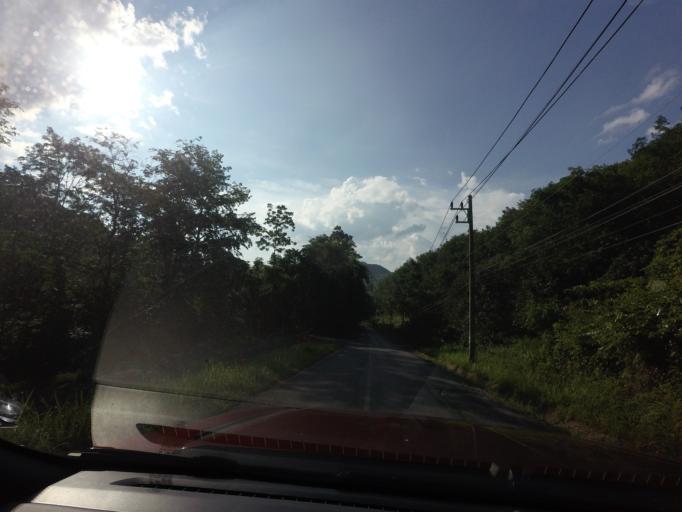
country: TH
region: Yala
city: Than To
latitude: 6.1529
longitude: 101.2810
